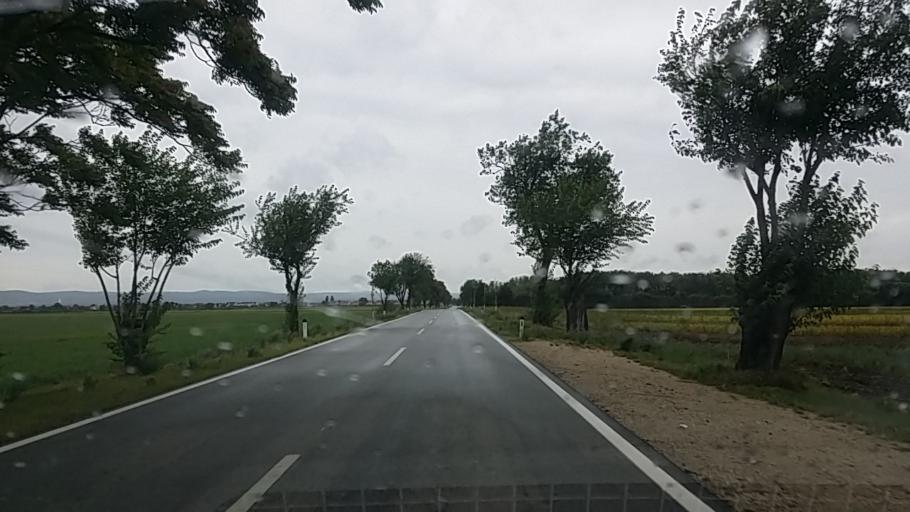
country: AT
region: Burgenland
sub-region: Eisenstadt-Umgebung
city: Sankt Margarethen im Burgenland
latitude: 47.7842
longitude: 16.6170
